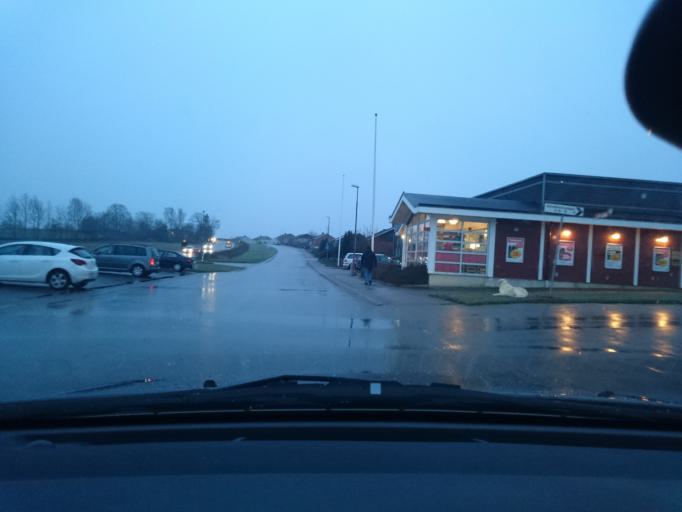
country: SE
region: Skane
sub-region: Bastads Kommun
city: Forslov
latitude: 56.3479
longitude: 12.8164
